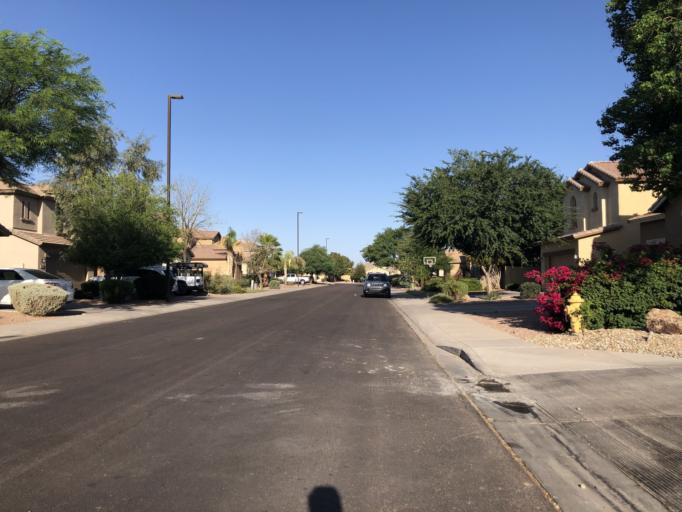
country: US
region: Arizona
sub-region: Maricopa County
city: Queen Creek
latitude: 33.2259
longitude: -111.7142
